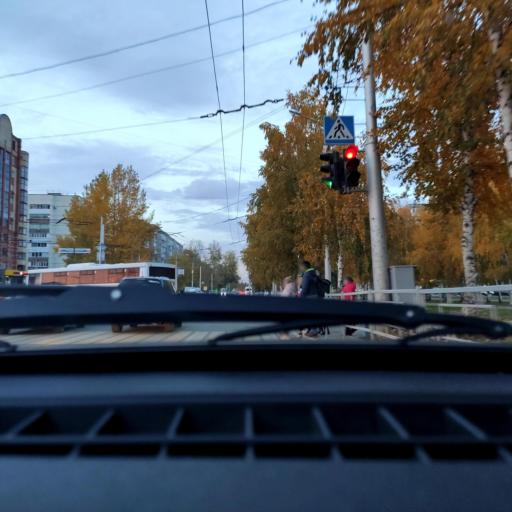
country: RU
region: Bashkortostan
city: Ufa
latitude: 54.7799
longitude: 56.1245
